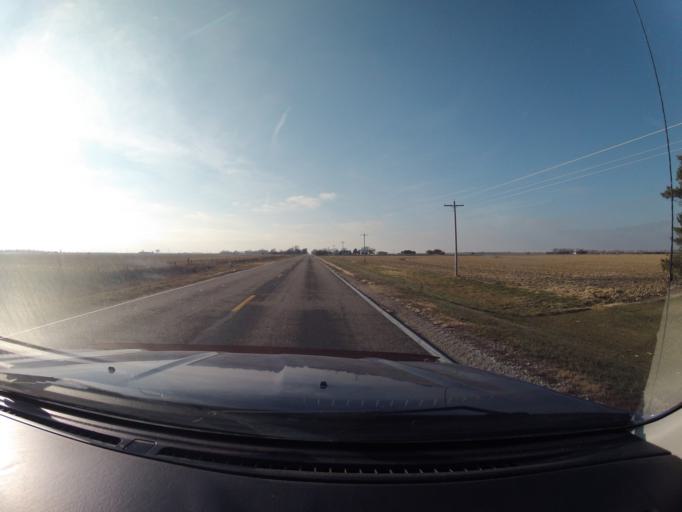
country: US
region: Nebraska
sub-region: Buffalo County
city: Kearney
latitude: 40.6410
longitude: -99.0746
